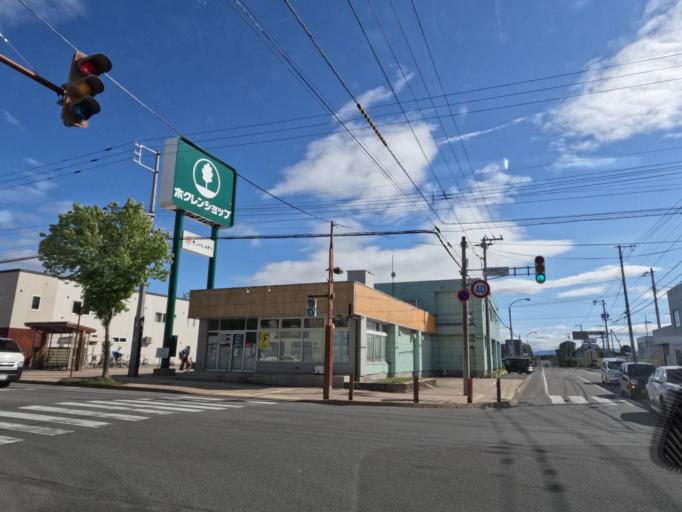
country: JP
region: Hokkaido
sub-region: Asahikawa-shi
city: Asahikawa
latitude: 43.6976
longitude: 142.5077
